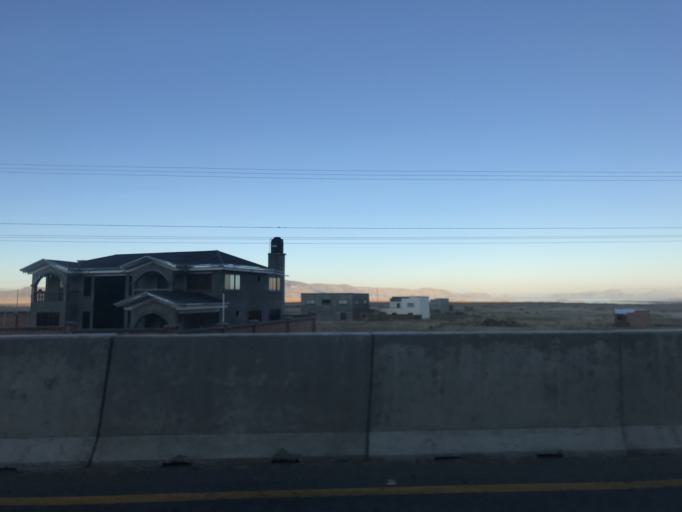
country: BO
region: La Paz
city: Batallas
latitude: -16.2519
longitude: -68.5684
